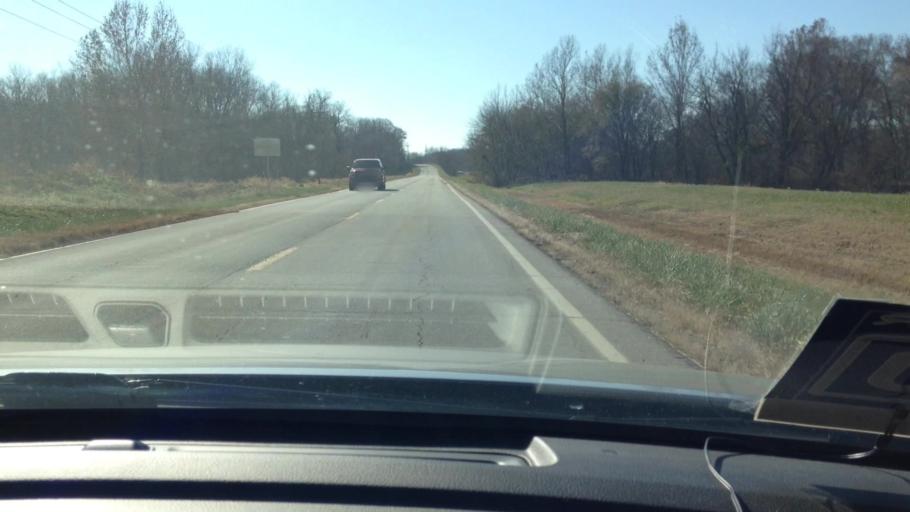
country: US
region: Missouri
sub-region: Platte County
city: Platte City
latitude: 39.4848
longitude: -94.8070
